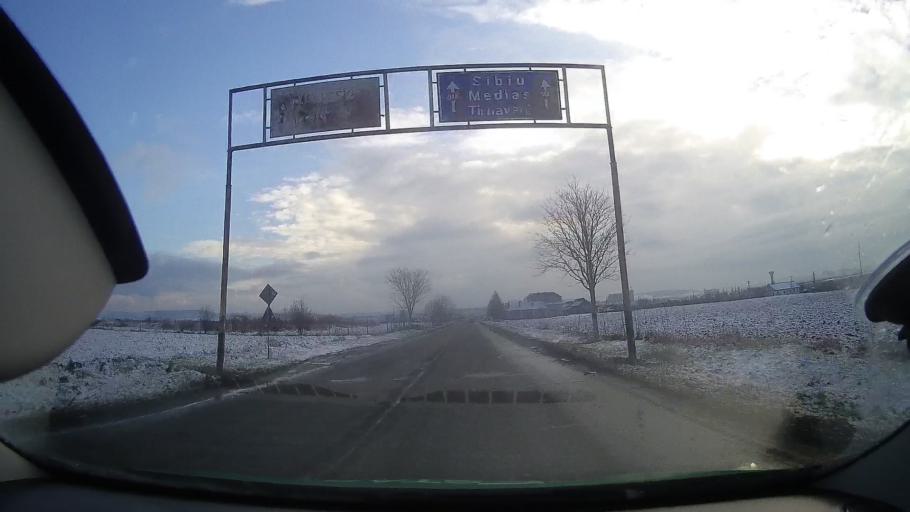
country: RO
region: Mures
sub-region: Comuna Iernut
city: Iernut
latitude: 46.4424
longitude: 24.2518
